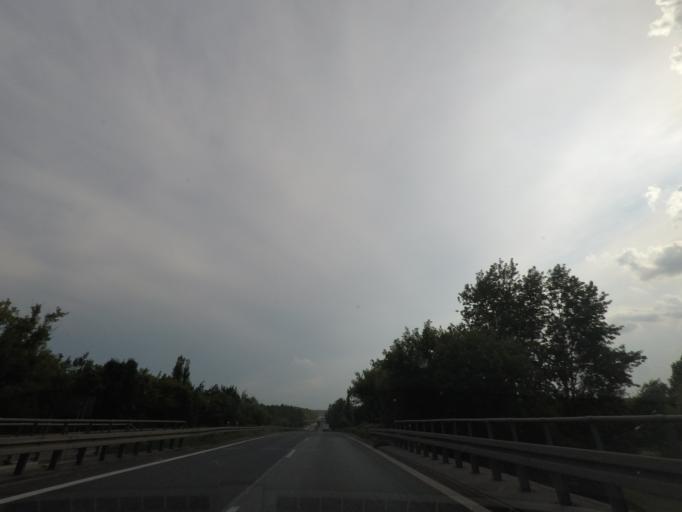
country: PL
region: Silesian Voivodeship
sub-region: Dabrowa Gornicza
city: Dabrowa Gornicza
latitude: 50.3307
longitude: 19.2436
